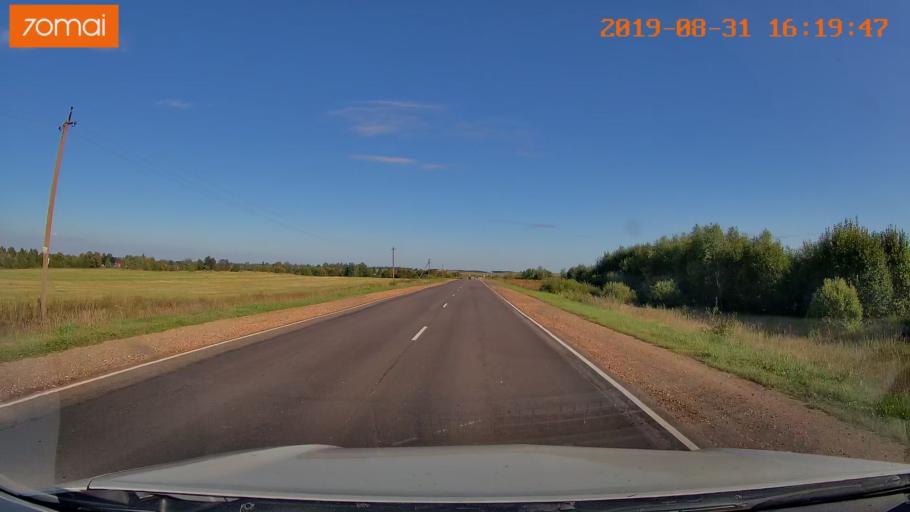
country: RU
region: Kaluga
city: Nikola-Lenivets
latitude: 54.5267
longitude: 35.5867
